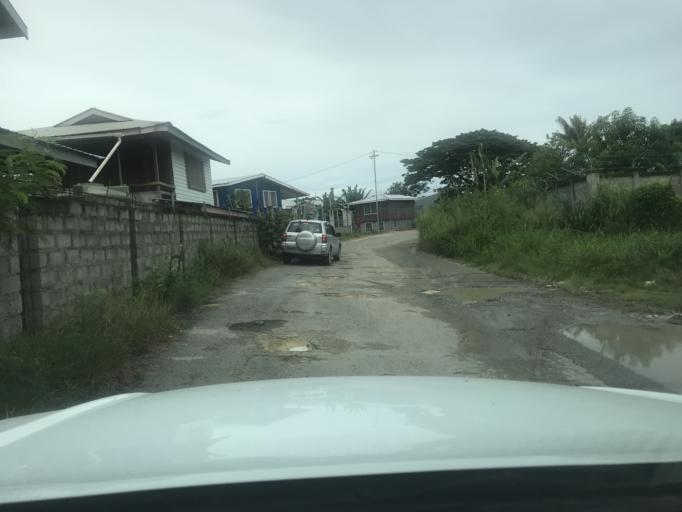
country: SB
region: Guadalcanal
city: Honiara
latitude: -9.4319
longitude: 160.0377
